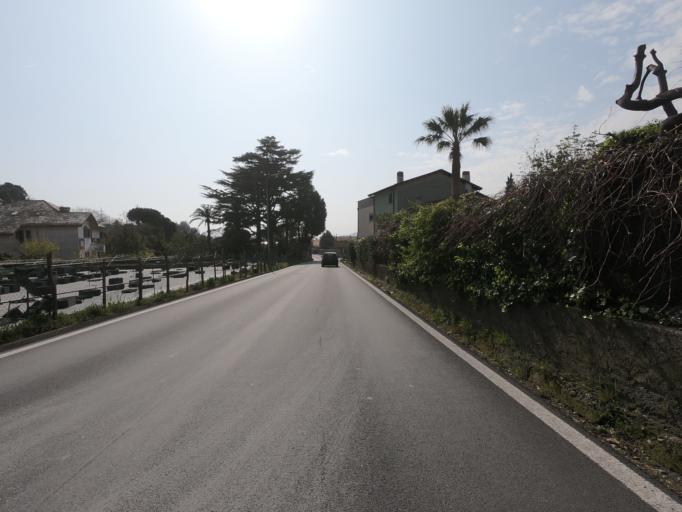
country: IT
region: Liguria
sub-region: Provincia di Savona
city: Cisano
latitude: 44.0861
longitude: 8.1486
